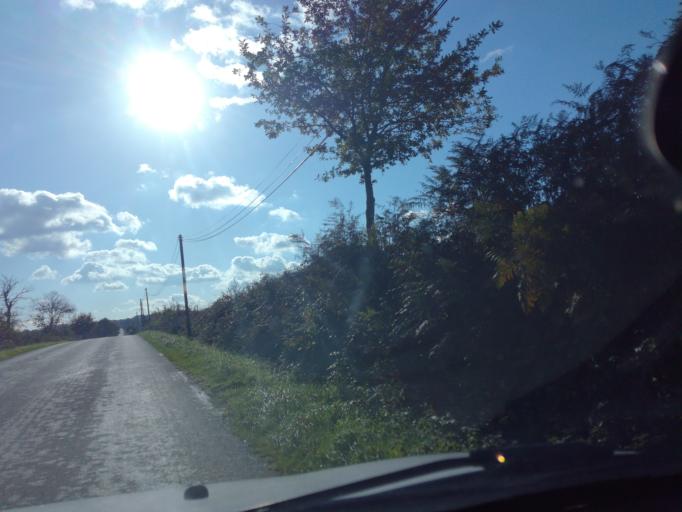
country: FR
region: Brittany
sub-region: Departement d'Ille-et-Vilaine
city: Chavagne
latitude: 48.0442
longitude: -1.8059
